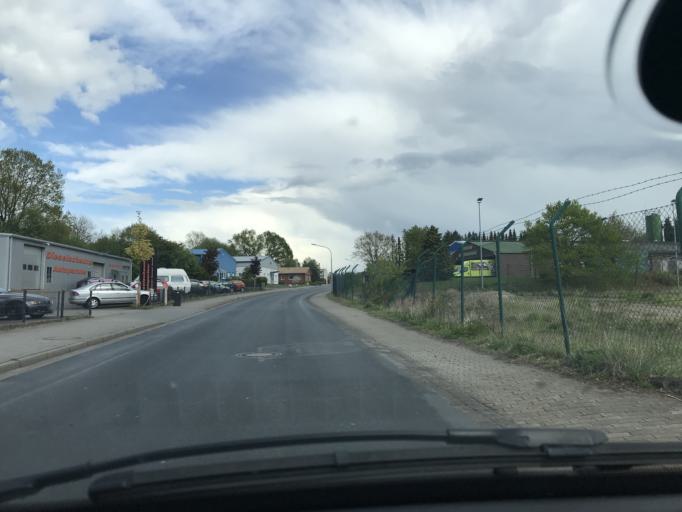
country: DE
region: Lower Saxony
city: Harsefeld
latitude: 53.4627
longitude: 9.5216
